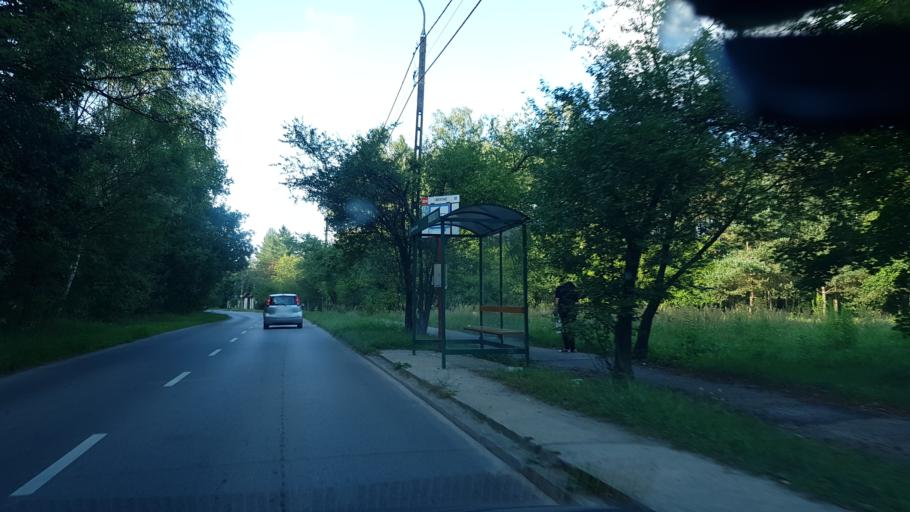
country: PL
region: Masovian Voivodeship
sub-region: Powiat piaseczynski
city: Konstancin-Jeziorna
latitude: 52.0684
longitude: 21.0999
